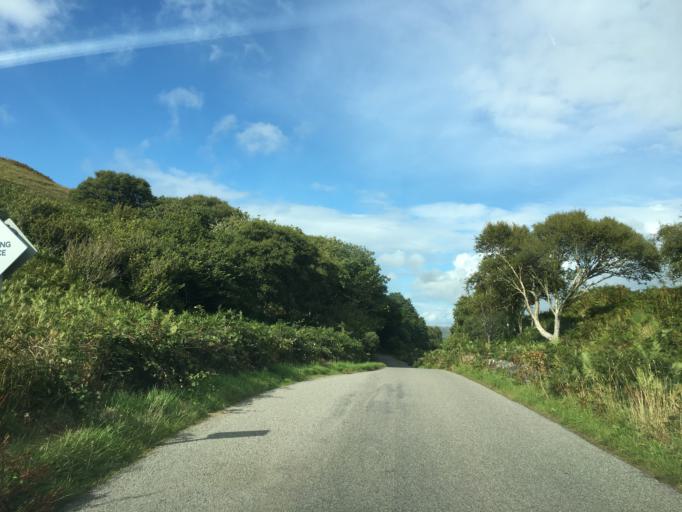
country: GB
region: Scotland
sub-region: Argyll and Bute
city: Oban
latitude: 56.2760
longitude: -5.6258
